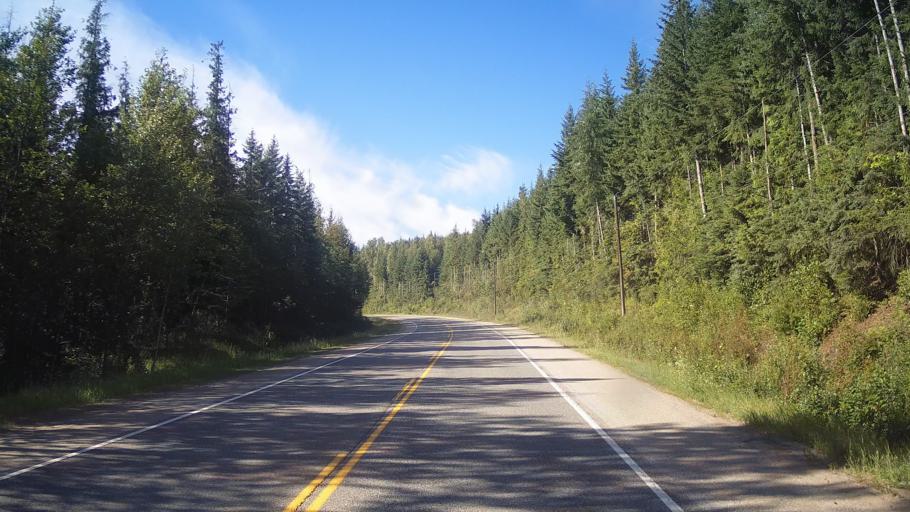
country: CA
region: British Columbia
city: Chase
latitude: 51.6375
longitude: -119.6966
